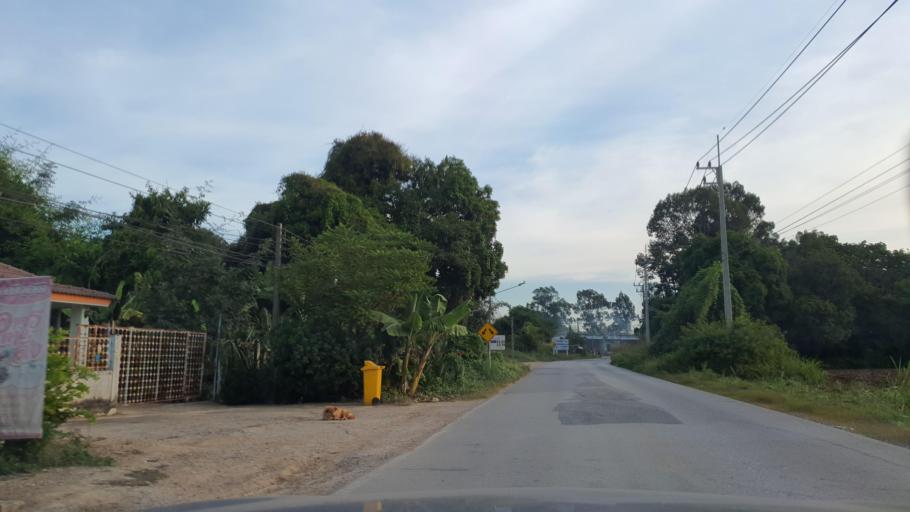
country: TH
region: Nakhon Sawan
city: Nakhon Sawan
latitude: 15.6653
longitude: 100.0611
